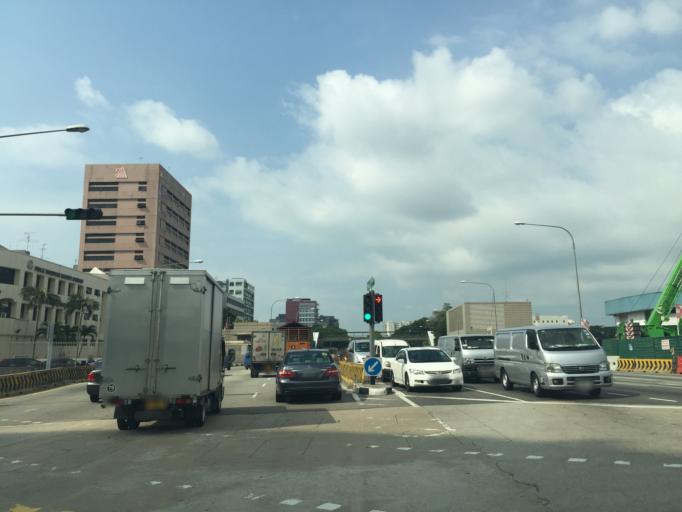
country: SG
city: Singapore
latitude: 1.3269
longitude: 103.8903
